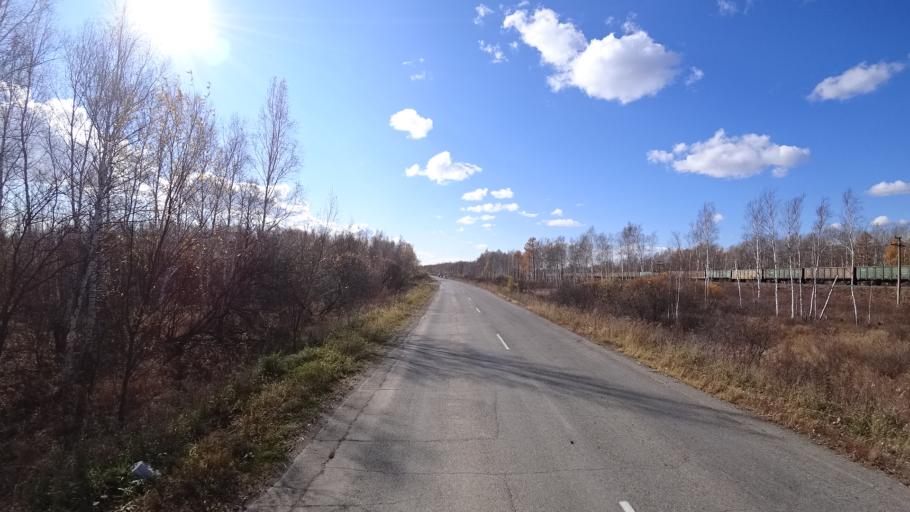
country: RU
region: Khabarovsk Krai
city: Amursk
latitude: 50.1128
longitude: 136.5215
